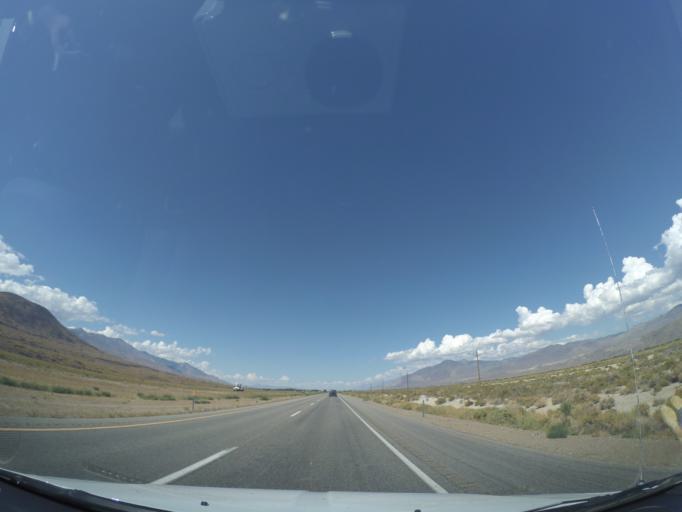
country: US
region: California
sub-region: Inyo County
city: Big Pine
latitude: 37.0991
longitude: -118.2506
